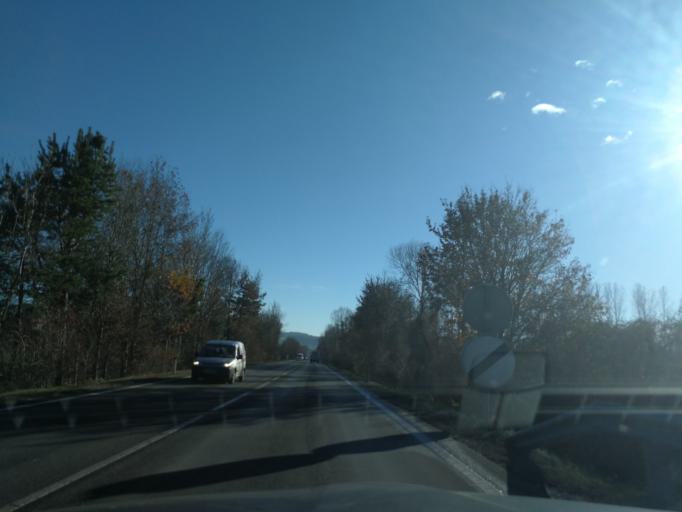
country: AT
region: Styria
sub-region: Politischer Bezirk Weiz
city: Hofstatten an der Raab
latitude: 47.0799
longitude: 15.7399
